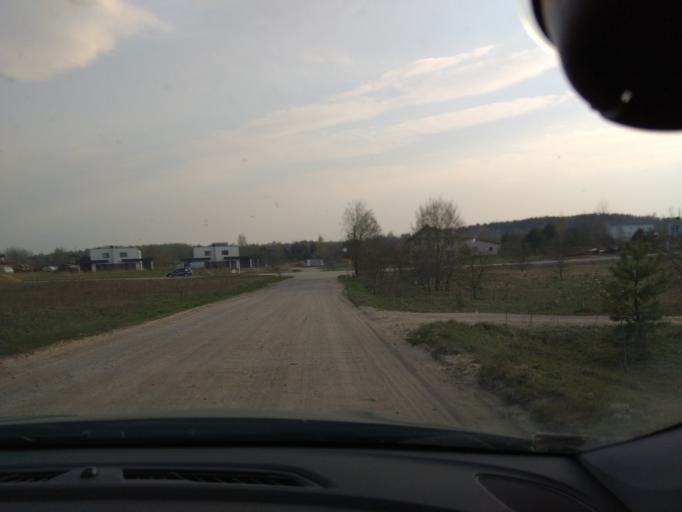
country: LT
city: Baltoji Voke
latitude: 54.5932
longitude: 25.1591
